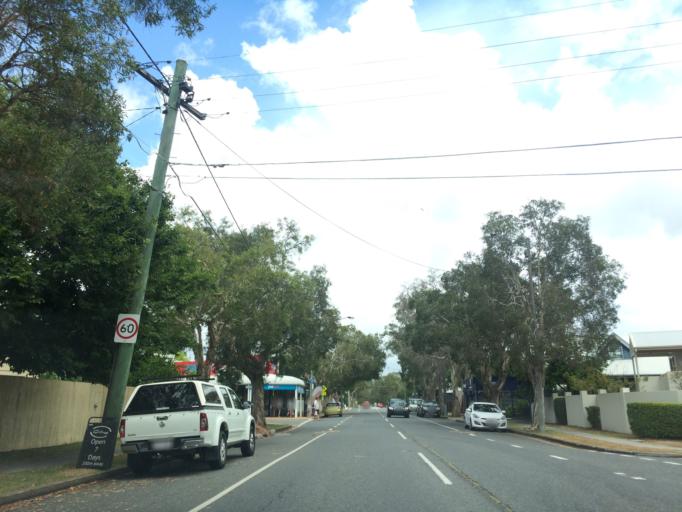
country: AU
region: Queensland
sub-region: Brisbane
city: Balmoral
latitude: -27.4604
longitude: 153.0632
